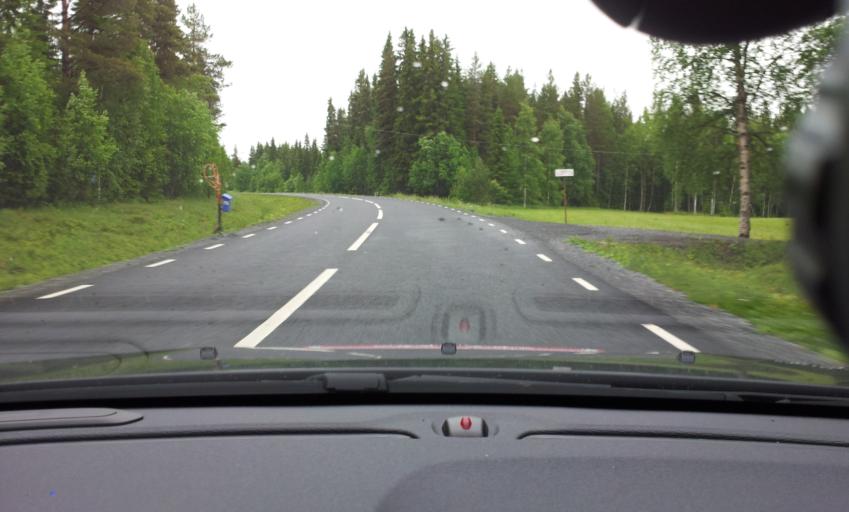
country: SE
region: Jaemtland
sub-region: Stroemsunds Kommun
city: Stroemsund
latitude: 63.6683
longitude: 15.1306
